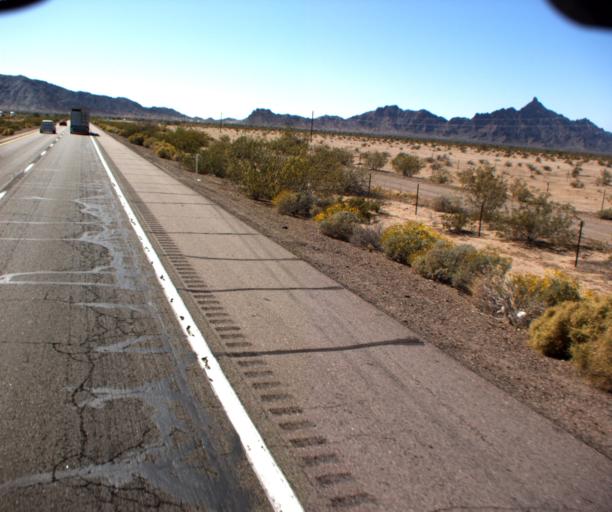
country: US
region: Arizona
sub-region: Yuma County
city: Wellton
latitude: 32.7363
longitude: -113.7005
